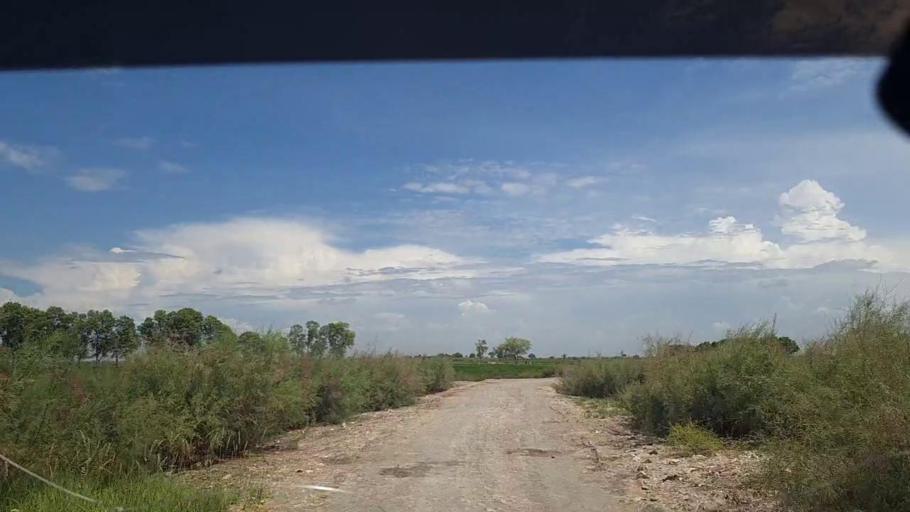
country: PK
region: Sindh
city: Ghauspur
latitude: 28.1495
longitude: 68.9664
